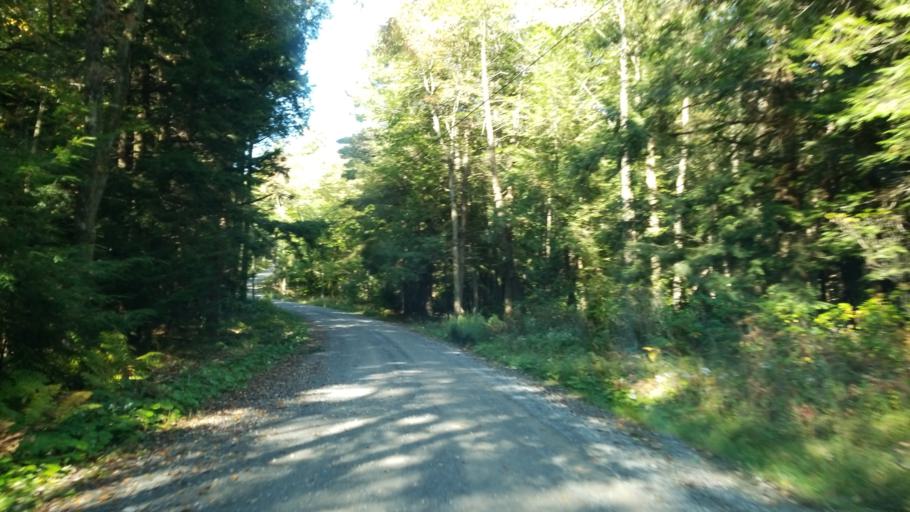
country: US
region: Pennsylvania
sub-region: Clearfield County
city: Hyde
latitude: 41.0888
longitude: -78.5355
